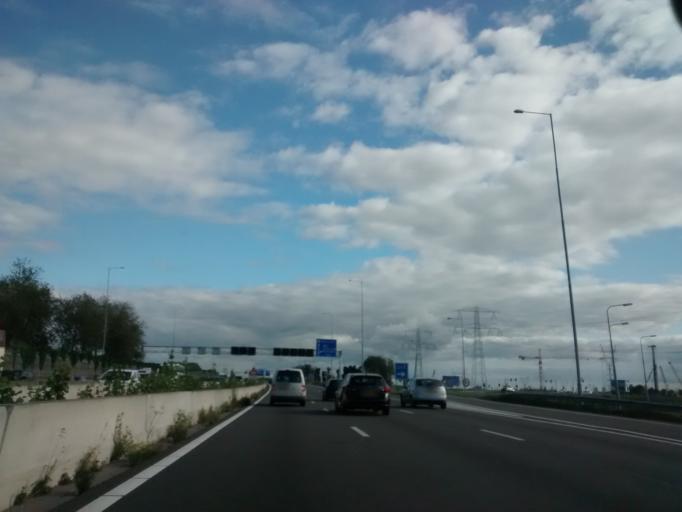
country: NL
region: North Holland
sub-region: Gemeente Weesp
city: Weesp
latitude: 52.3285
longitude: 5.0582
